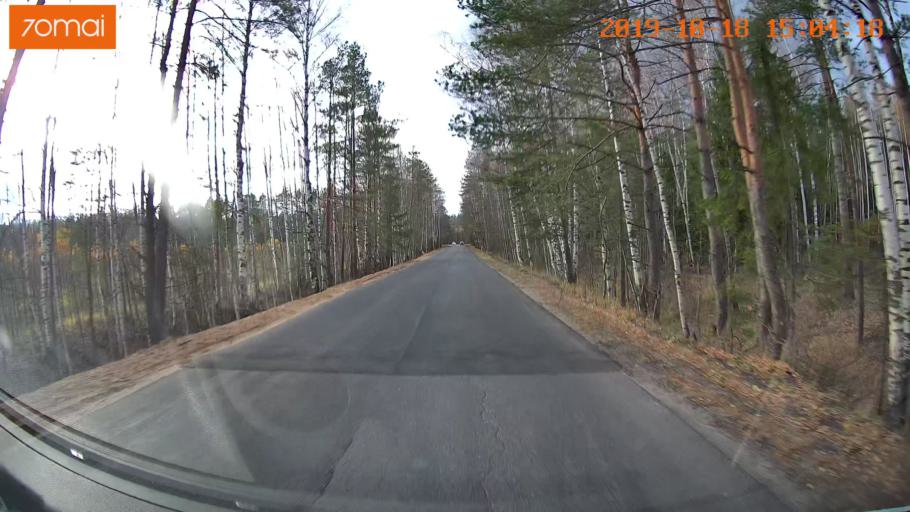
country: RU
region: Vladimir
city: Kurlovo
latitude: 55.5043
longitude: 40.5761
